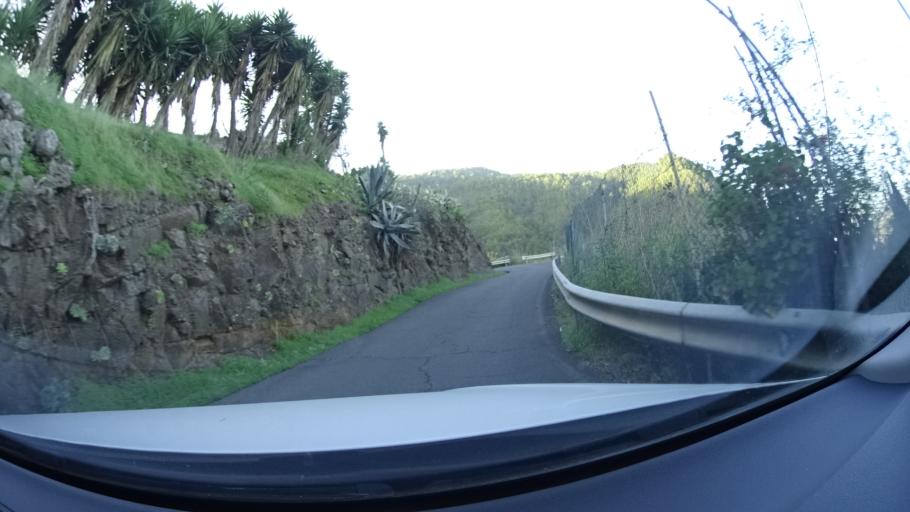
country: ES
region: Canary Islands
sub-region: Provincia de Las Palmas
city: Artenara
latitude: 28.0468
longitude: -15.6706
